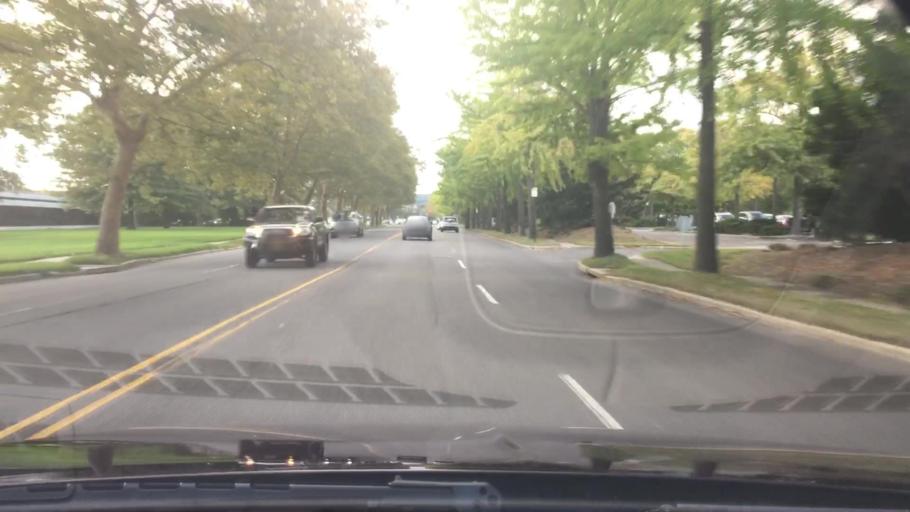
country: US
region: New York
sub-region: Suffolk County
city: Melville
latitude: 40.7707
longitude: -73.4169
